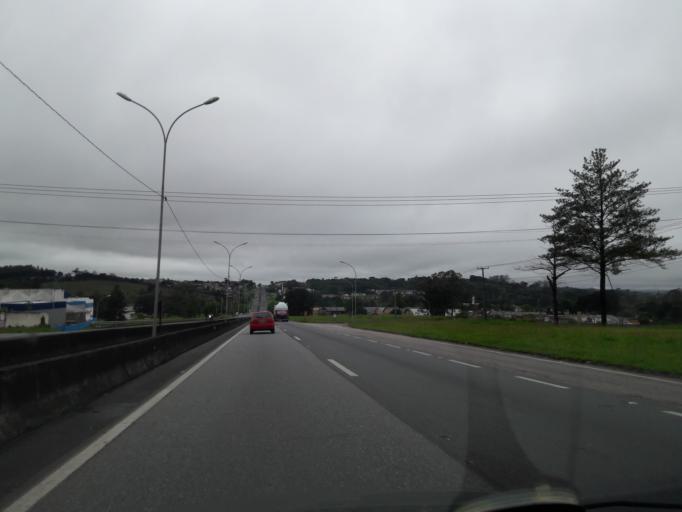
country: BR
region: Parana
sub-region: Quatro Barras
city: Quatro Barras
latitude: -25.3716
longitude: -49.1316
